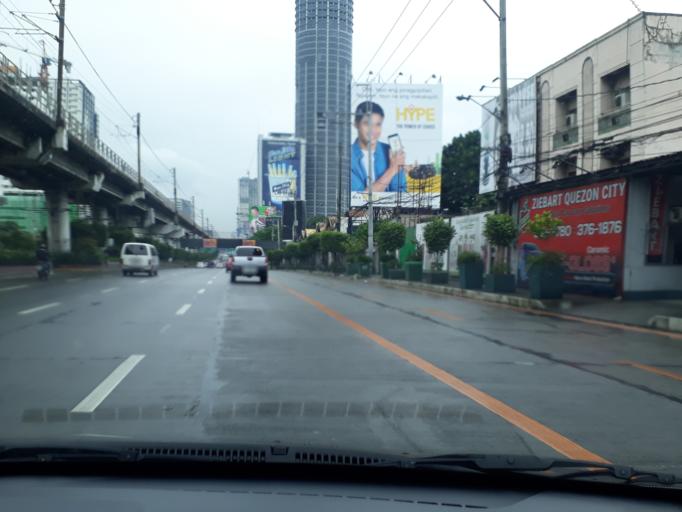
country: PH
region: Calabarzon
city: Bagong Pagasa
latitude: 14.6492
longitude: 121.0340
